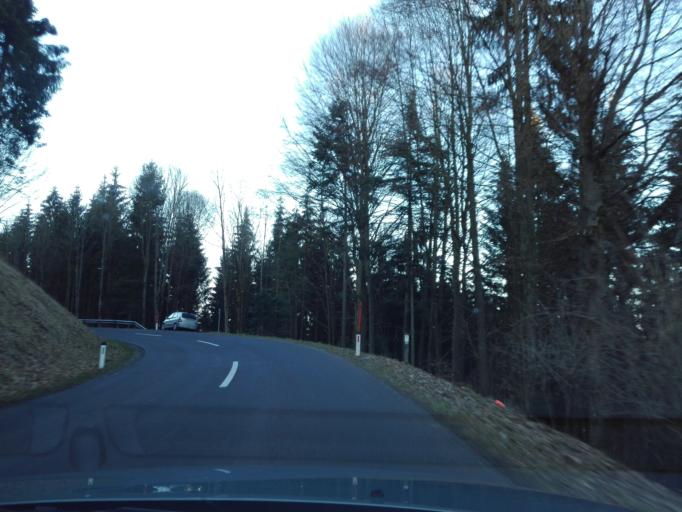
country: AT
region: Upper Austria
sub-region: Politischer Bezirk Rohrbach
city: Kleinzell im Muehlkreis
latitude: 48.3994
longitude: 13.9346
